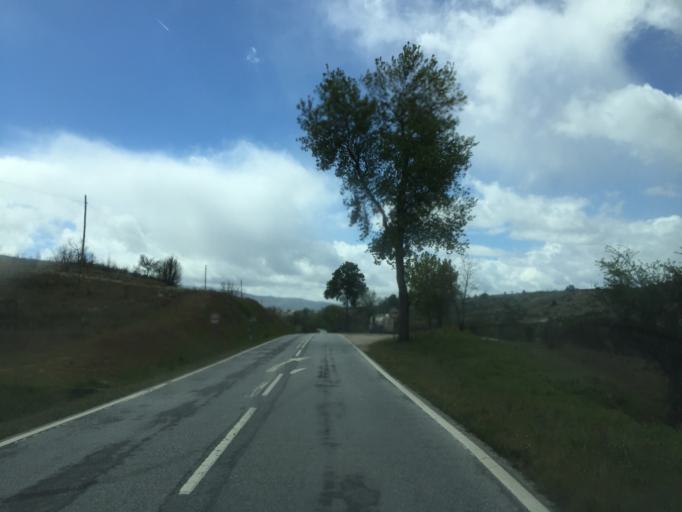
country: PT
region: Guarda
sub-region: Celorico da Beira
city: Celorico da Beira
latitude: 40.5760
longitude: -7.4598
